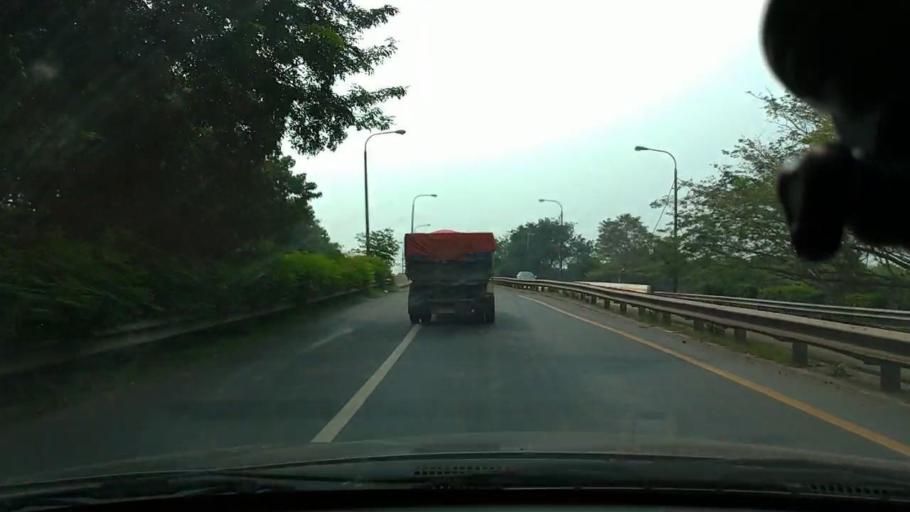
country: ID
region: Banten
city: Serang
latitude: -6.0891
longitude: 106.1448
